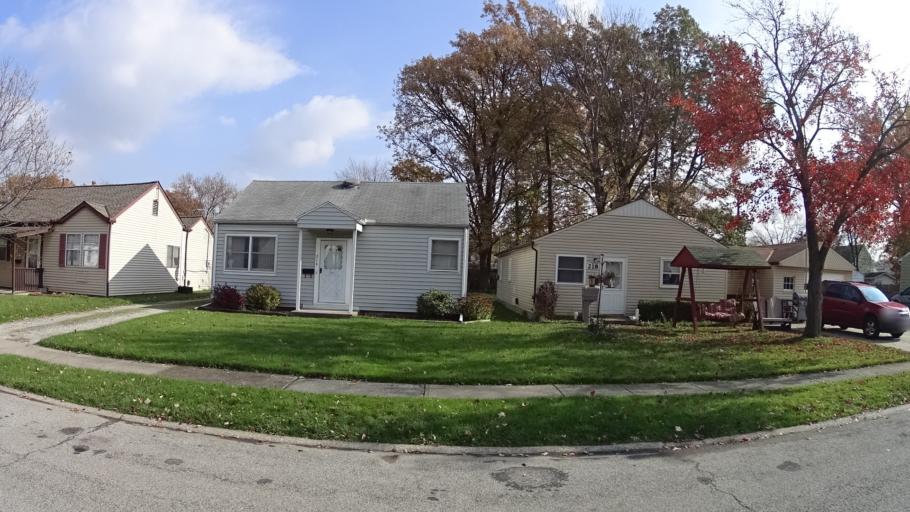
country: US
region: Ohio
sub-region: Lorain County
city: Elyria
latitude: 41.3682
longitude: -82.0850
